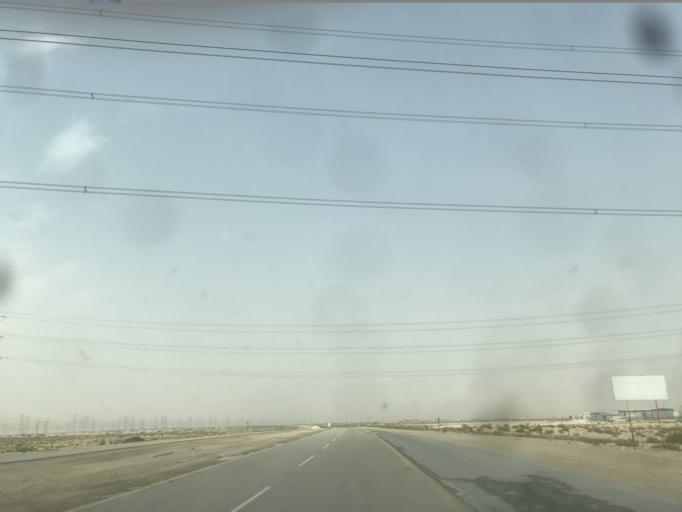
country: SA
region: Eastern Province
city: Abqaiq
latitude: 25.9107
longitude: 49.9626
